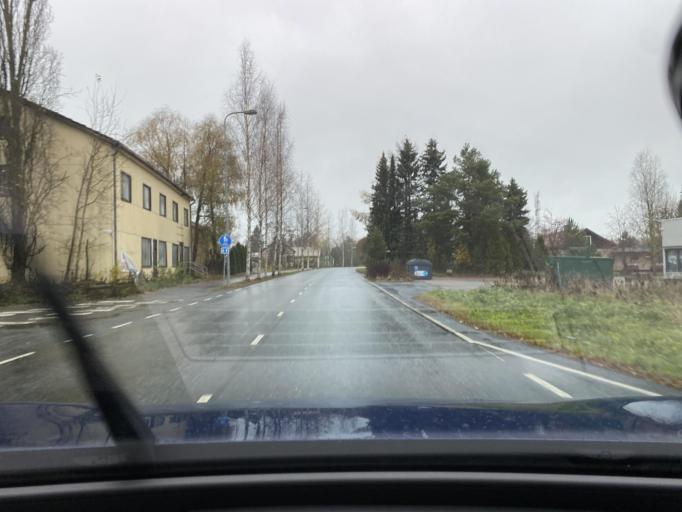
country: FI
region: Varsinais-Suomi
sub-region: Loimaa
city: Alastaro
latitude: 60.9462
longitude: 22.8649
